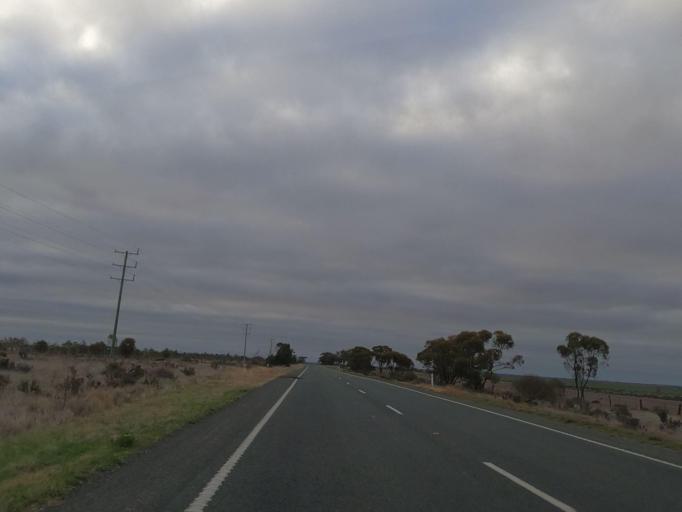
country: AU
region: Victoria
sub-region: Swan Hill
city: Swan Hill
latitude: -35.5732
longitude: 143.7869
